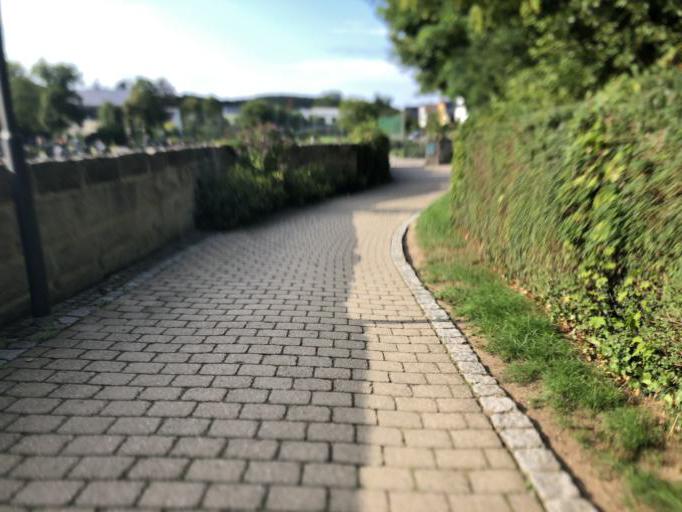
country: DE
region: Bavaria
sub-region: Regierungsbezirk Mittelfranken
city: Mohrendorf
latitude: 49.6401
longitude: 11.0019
